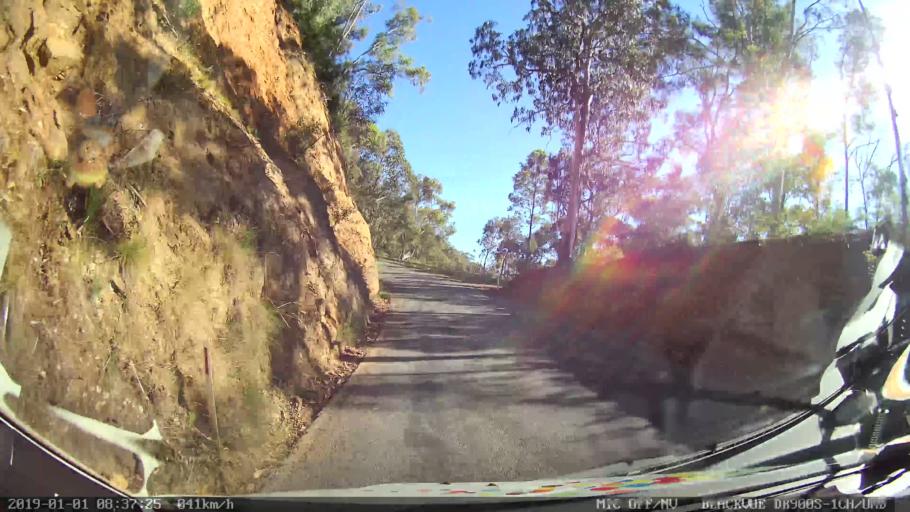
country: AU
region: New South Wales
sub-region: Snowy River
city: Jindabyne
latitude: -36.3383
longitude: 148.1962
